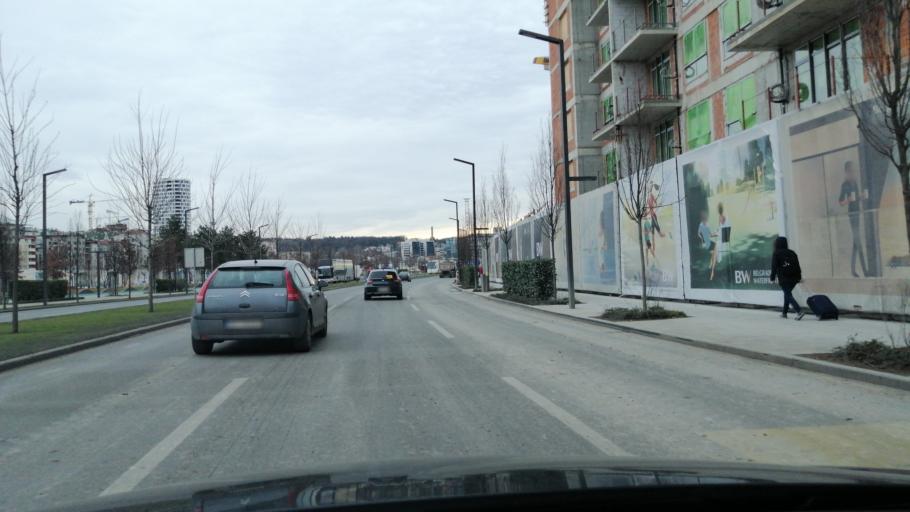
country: RS
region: Central Serbia
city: Belgrade
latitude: 44.8056
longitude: 20.4511
